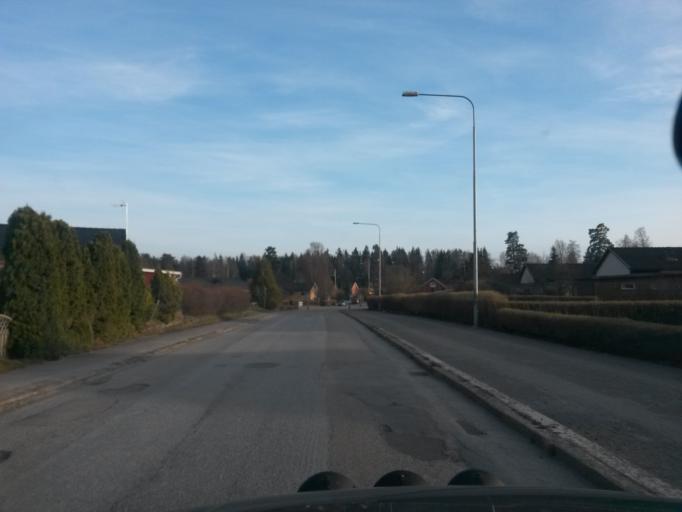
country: SE
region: OErebro
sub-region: Karlskoga Kommun
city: Karlskoga
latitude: 59.3100
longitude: 14.4944
